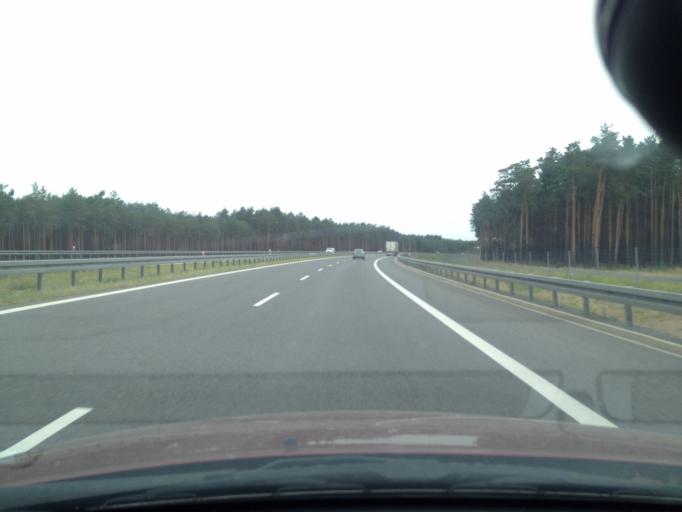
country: PL
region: Lubusz
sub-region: Powiat gorzowski
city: Deszczno
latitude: 52.6168
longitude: 15.3911
